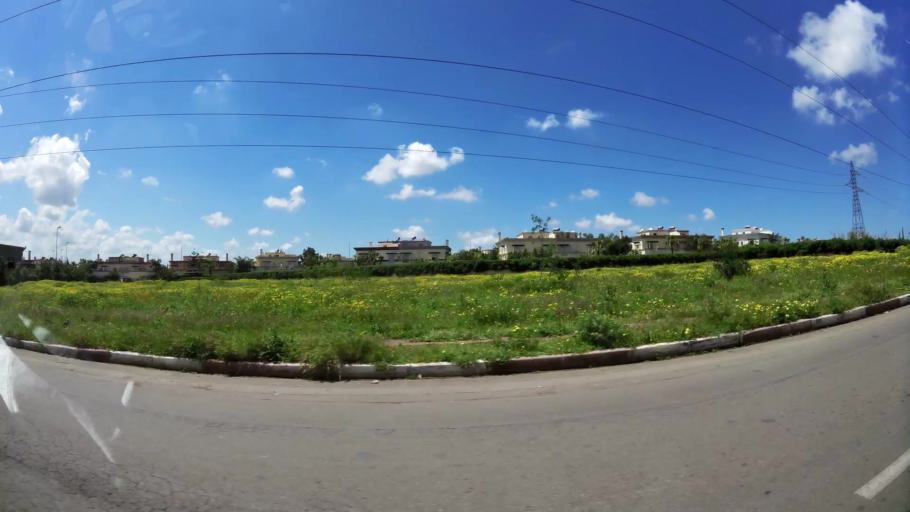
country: MA
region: Grand Casablanca
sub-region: Casablanca
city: Casablanca
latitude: 33.5285
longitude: -7.6172
